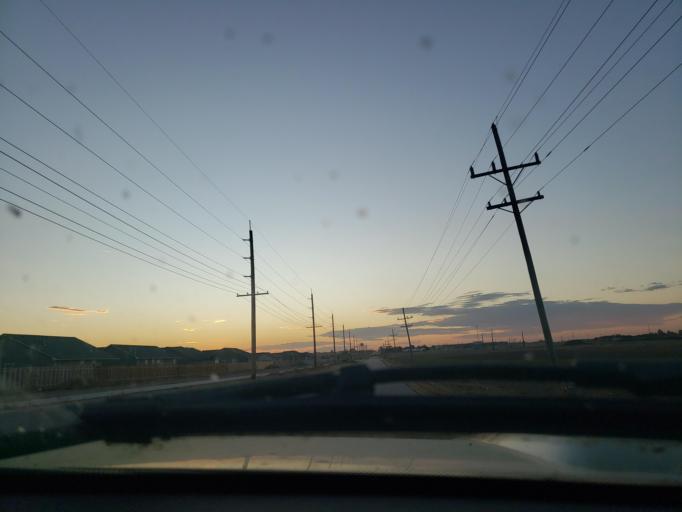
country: US
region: Kansas
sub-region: Finney County
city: Garden City
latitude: 37.9891
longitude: -100.8185
